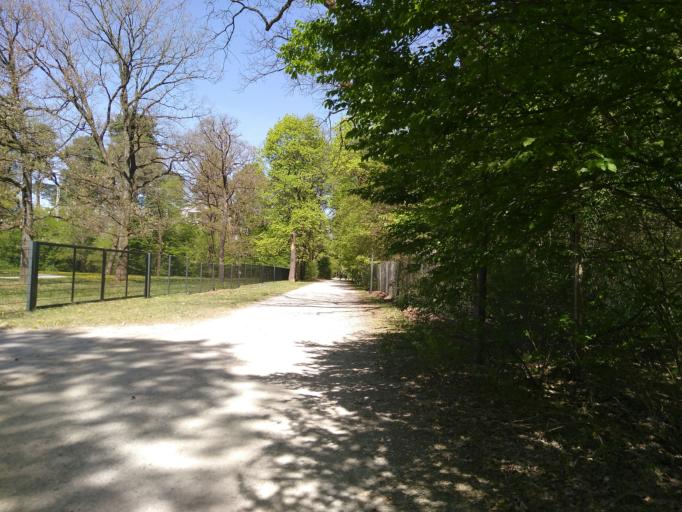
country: DE
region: Bavaria
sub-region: Upper Bavaria
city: Unterhaching
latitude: 48.0951
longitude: 11.6014
